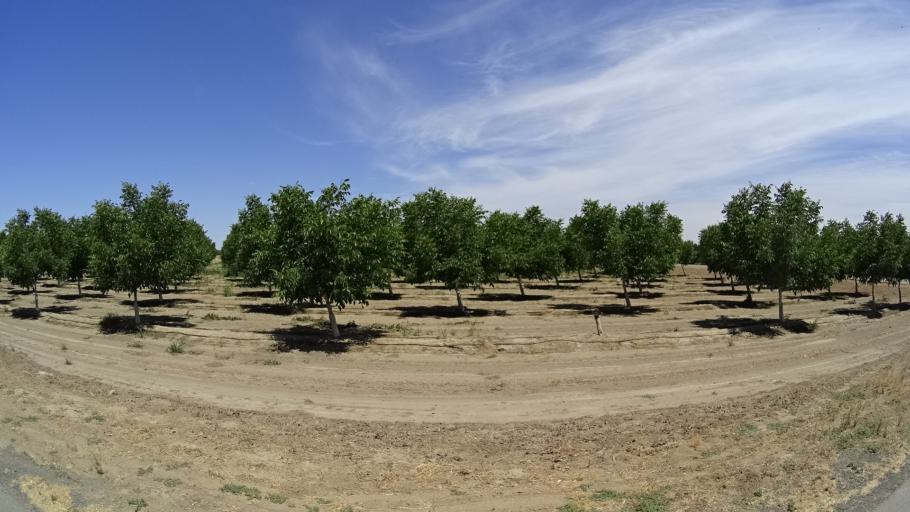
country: US
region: California
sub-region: Kings County
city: Lemoore
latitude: 36.3426
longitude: -119.7630
